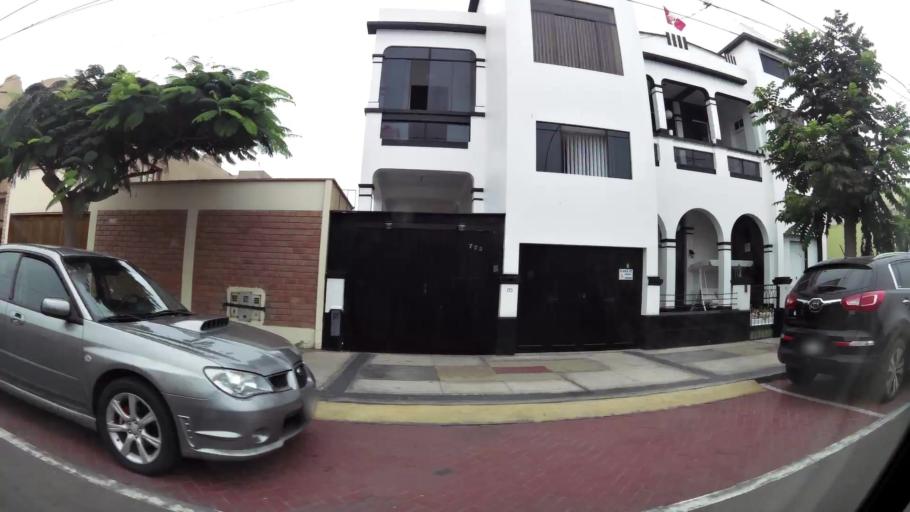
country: PE
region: Callao
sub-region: Callao
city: Callao
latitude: -12.0696
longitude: -77.1598
